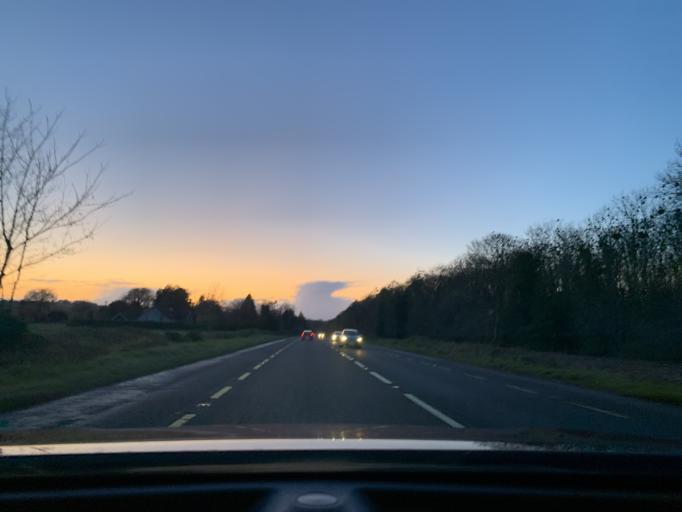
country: IE
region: Connaught
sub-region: Roscommon
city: Boyle
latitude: 53.9700
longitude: -8.2119
